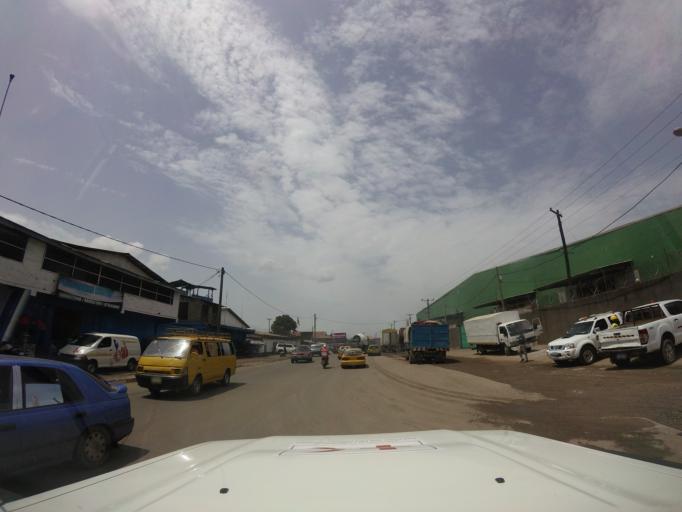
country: LR
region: Montserrado
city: Monrovia
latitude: 6.3435
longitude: -10.7904
